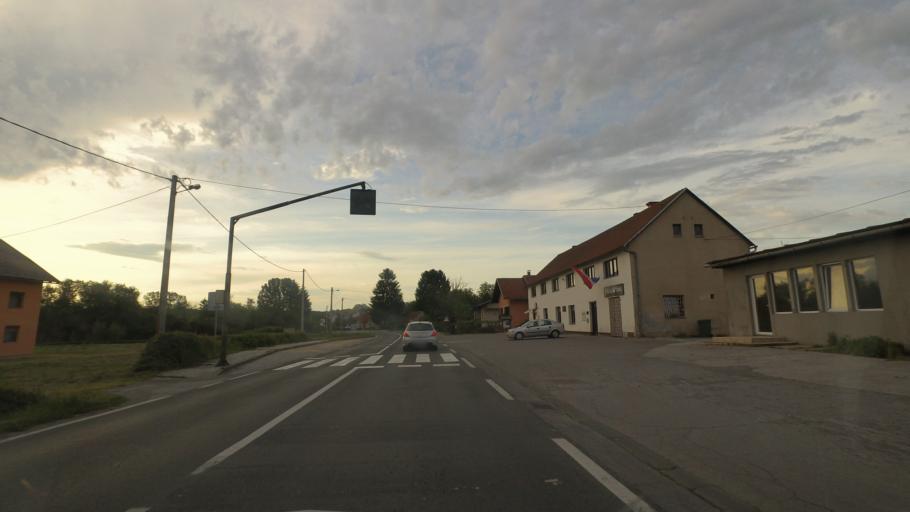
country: HR
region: Karlovacka
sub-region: Grad Karlovac
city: Karlovac
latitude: 45.4266
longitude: 15.6059
